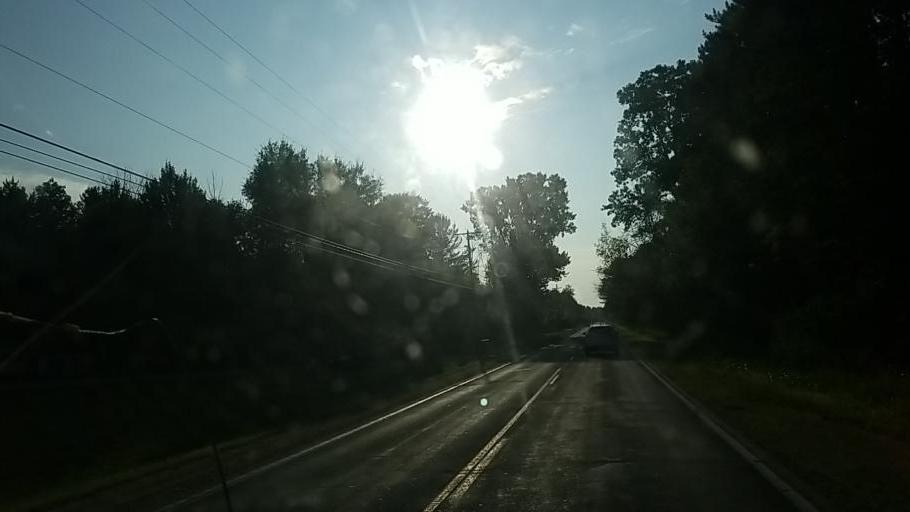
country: US
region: Michigan
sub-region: Montcalm County
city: Stanton
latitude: 43.2499
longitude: -85.0919
